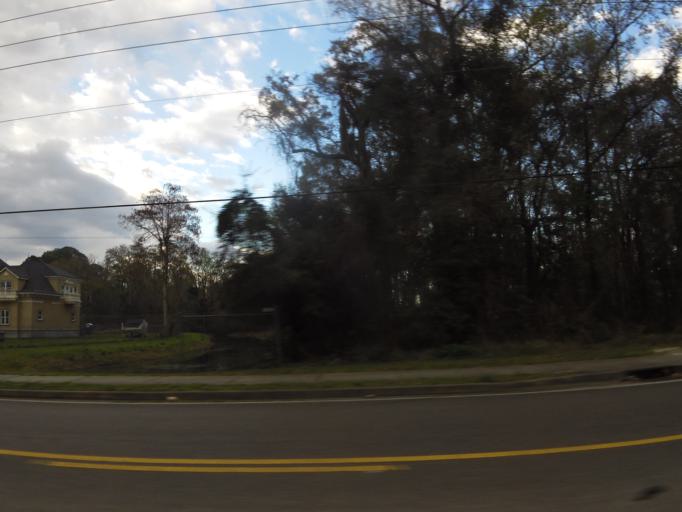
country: US
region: Florida
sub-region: Saint Johns County
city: Fruit Cove
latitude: 30.1950
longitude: -81.5832
